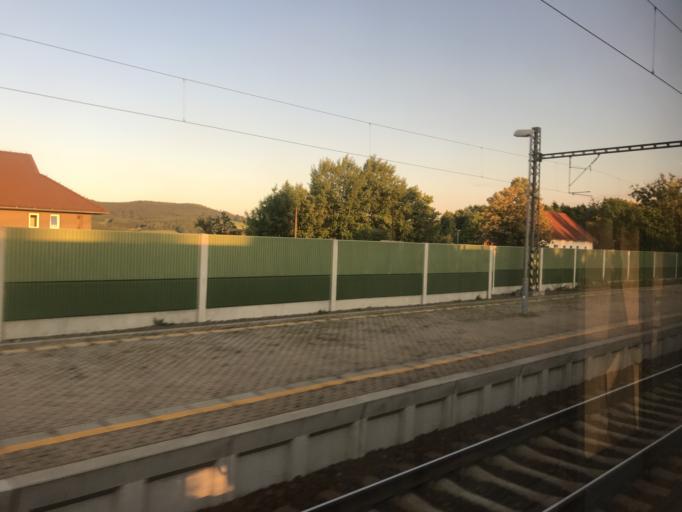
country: CZ
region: Central Bohemia
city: Votice
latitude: 49.6680
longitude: 14.6246
